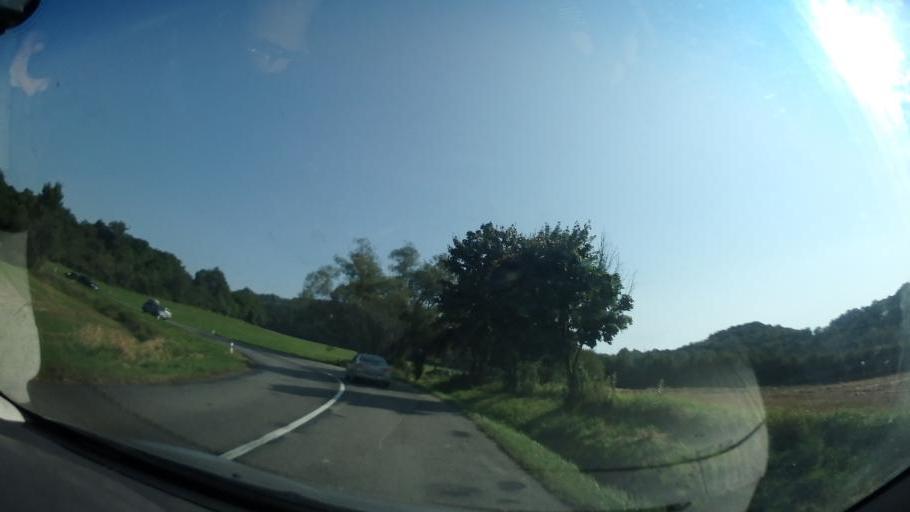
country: CZ
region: South Moravian
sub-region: Okres Brno-Venkov
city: Dolni Loucky
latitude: 49.4083
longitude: 16.3512
